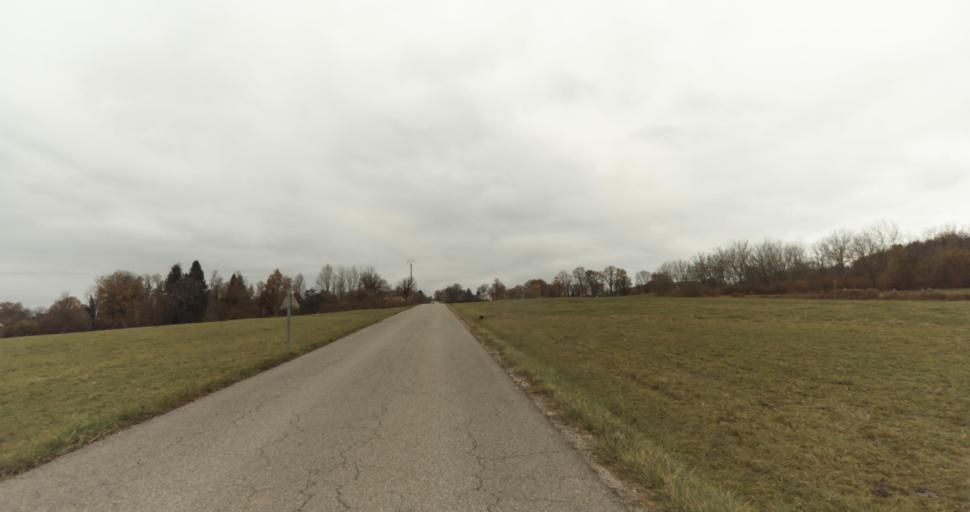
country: FR
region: Rhone-Alpes
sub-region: Departement de la Haute-Savoie
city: Allonzier-la-Caille
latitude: 45.9820
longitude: 6.1255
